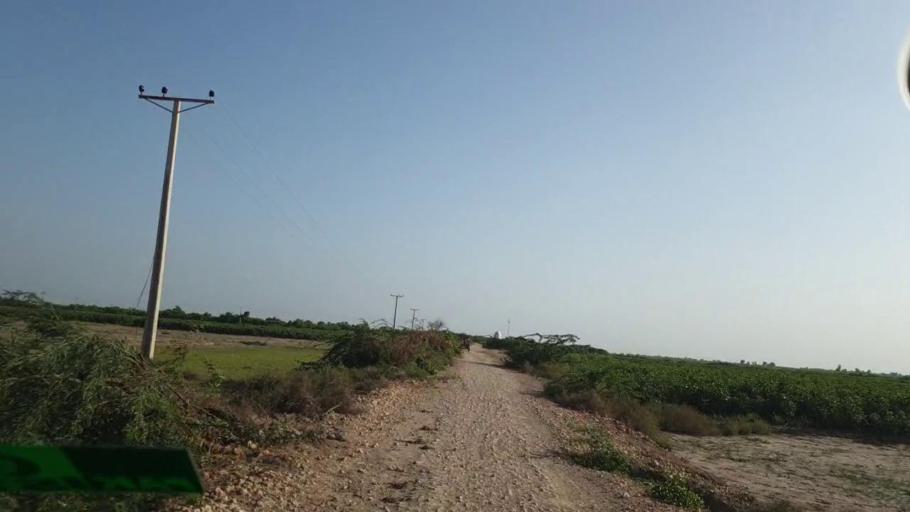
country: PK
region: Sindh
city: Naukot
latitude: 24.7394
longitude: 69.2477
